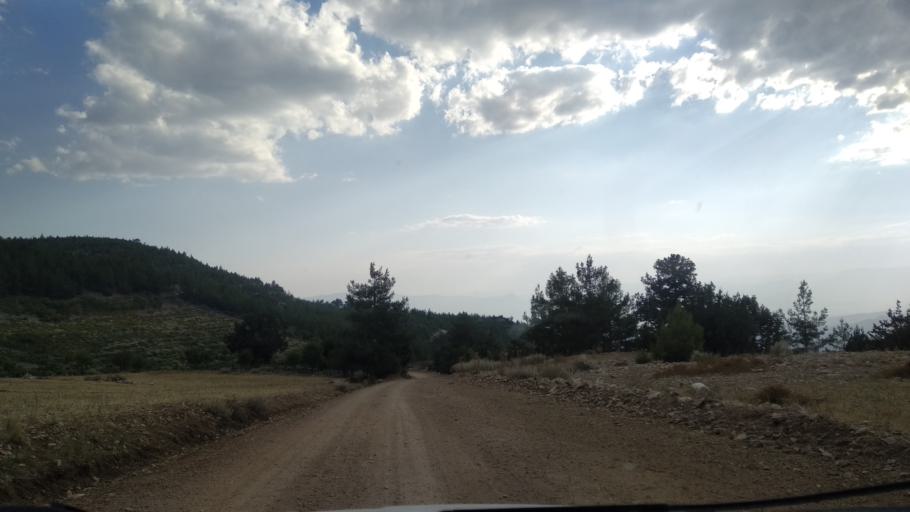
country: TR
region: Mersin
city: Sarikavak
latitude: 36.5908
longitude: 33.6779
